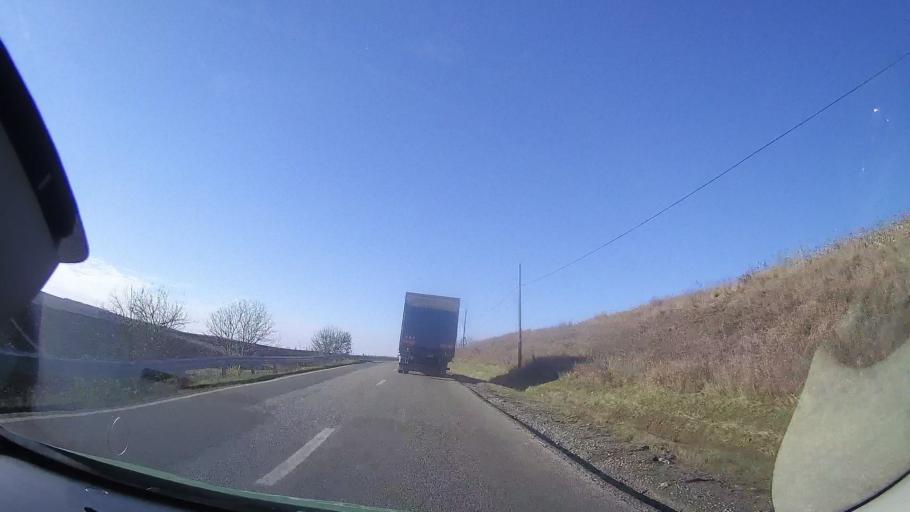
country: RO
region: Cluj
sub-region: Comuna Camarasu
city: Camarasu
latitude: 46.7931
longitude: 24.1154
